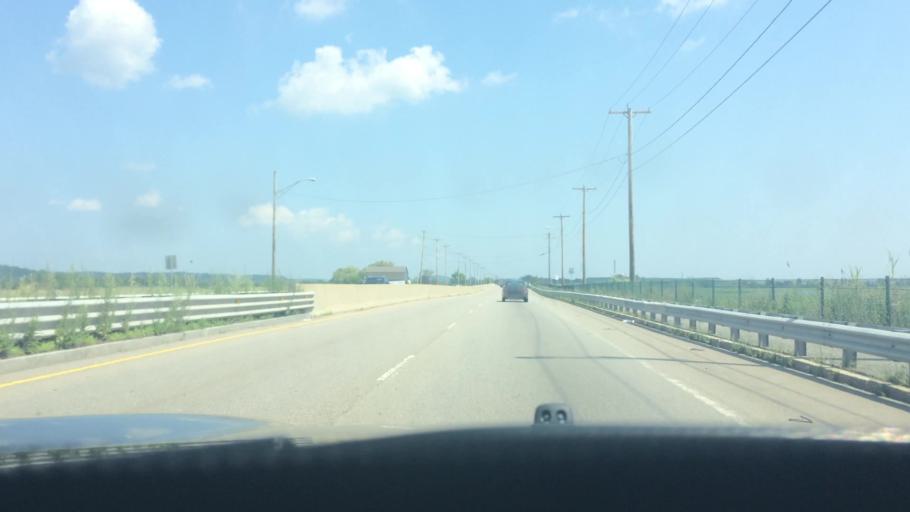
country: US
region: Massachusetts
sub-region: Suffolk County
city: Revere
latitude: 42.4262
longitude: -71.0008
